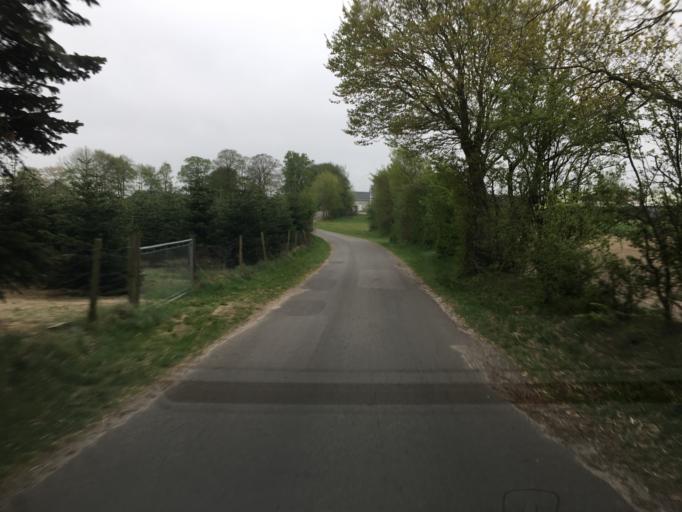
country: DK
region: South Denmark
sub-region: Aabenraa Kommune
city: Krusa
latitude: 54.8861
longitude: 9.3985
